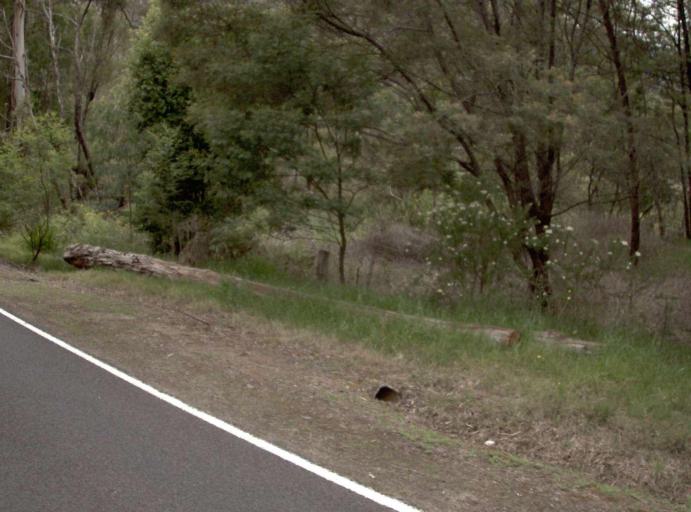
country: AU
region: New South Wales
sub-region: Bombala
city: Bombala
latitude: -37.4273
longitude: 149.1994
